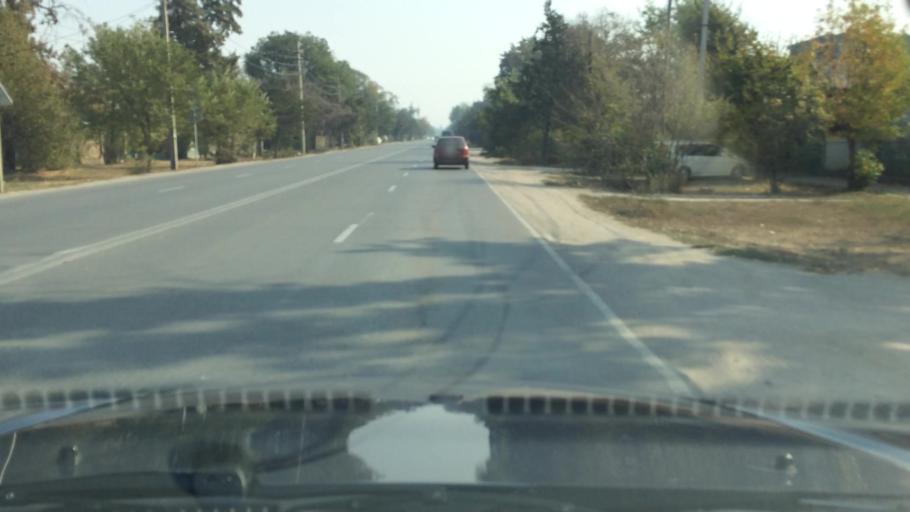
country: KG
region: Chuy
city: Lebedinovka
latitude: 42.8837
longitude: 74.6416
